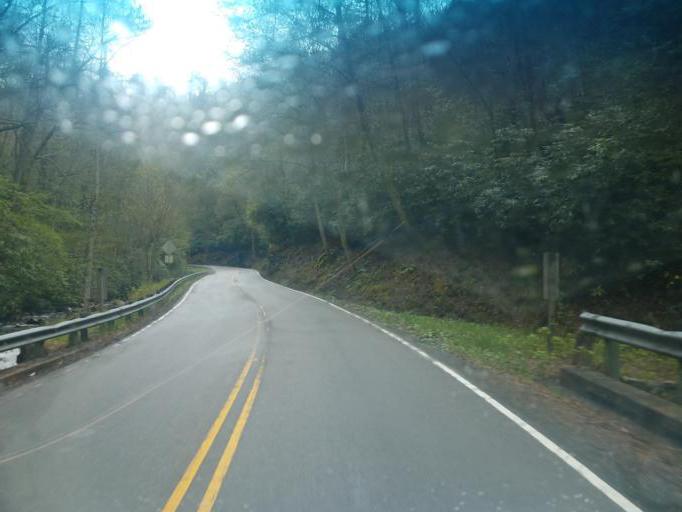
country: US
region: Virginia
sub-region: Washington County
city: Glade Spring
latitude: 36.6421
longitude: -81.7154
